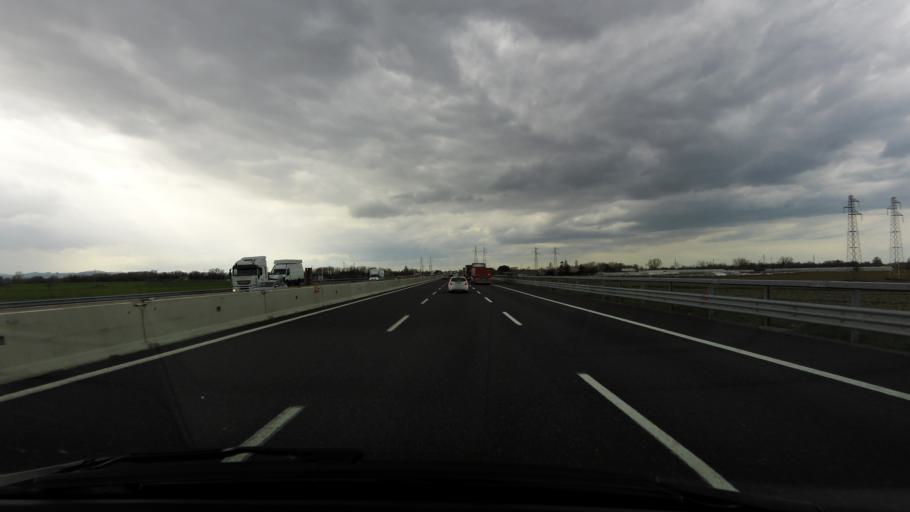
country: IT
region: Emilia-Romagna
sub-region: Provincia di Rimini
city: Santa Giustina
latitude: 44.0568
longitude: 12.5141
